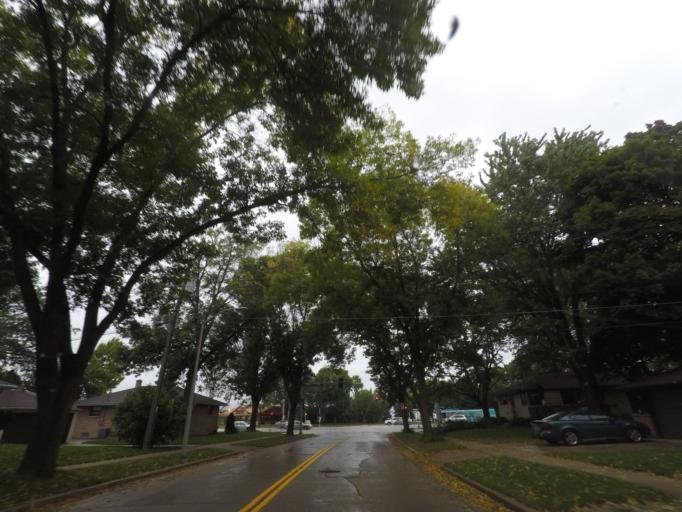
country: US
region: Wisconsin
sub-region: Milwaukee County
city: West Allis
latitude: 42.9961
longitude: -88.0410
